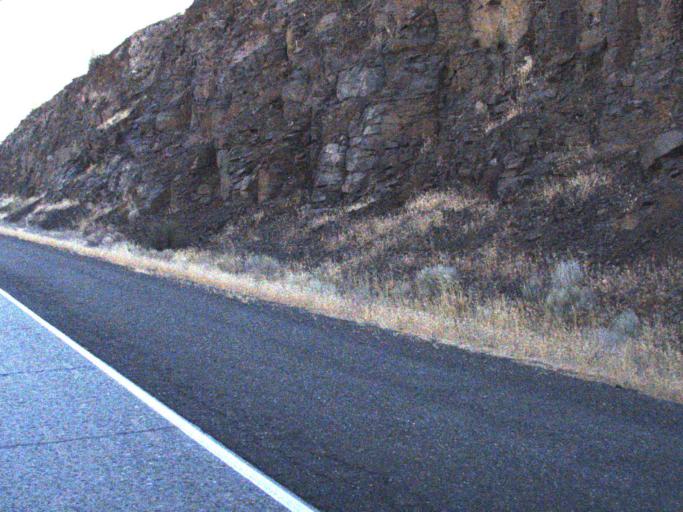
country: US
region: Washington
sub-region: Kittitas County
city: Kittitas
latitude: 46.8145
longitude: -120.3536
